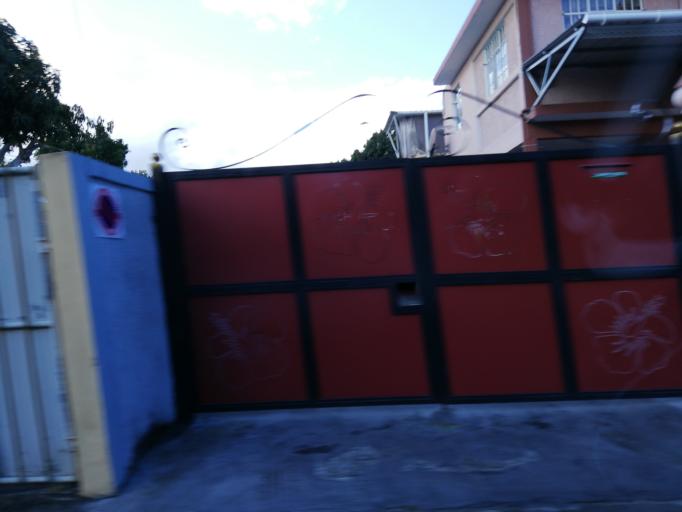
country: MU
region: Moka
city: Moka
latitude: -20.2214
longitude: 57.4716
